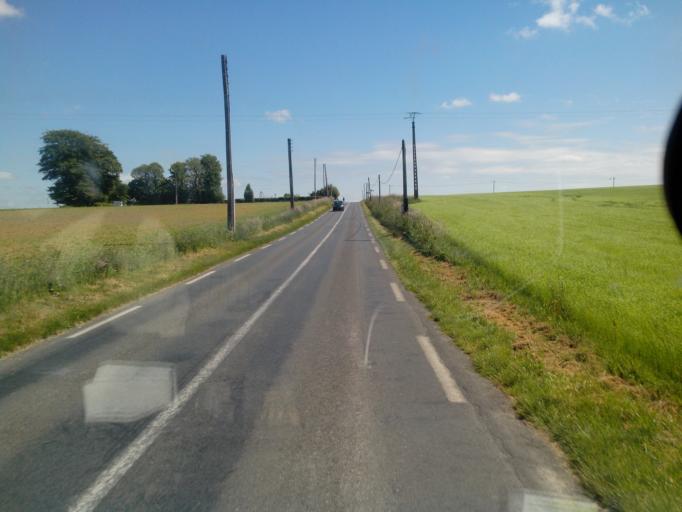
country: FR
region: Haute-Normandie
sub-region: Departement de la Seine-Maritime
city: Turretot
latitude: 49.6177
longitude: 0.2834
